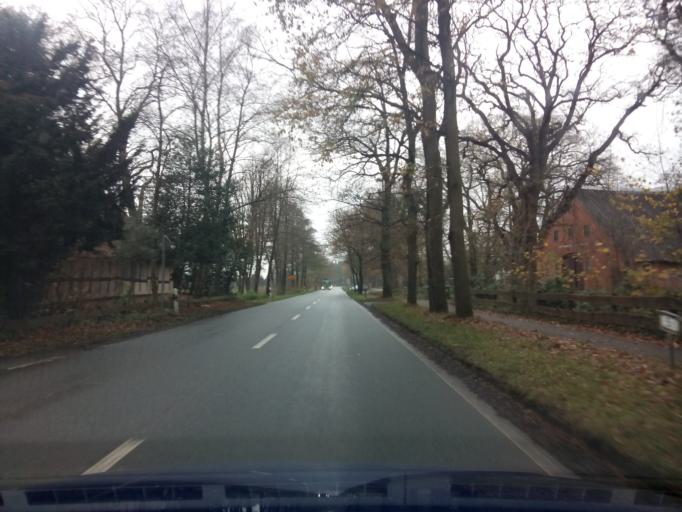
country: DE
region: Lower Saxony
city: Lilienthal
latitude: 53.1729
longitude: 8.8999
